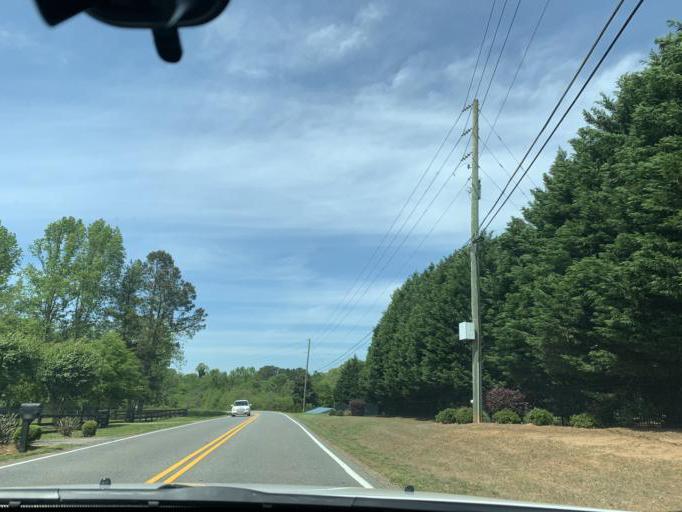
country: US
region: Georgia
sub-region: Forsyth County
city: Cumming
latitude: 34.2576
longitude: -84.1707
